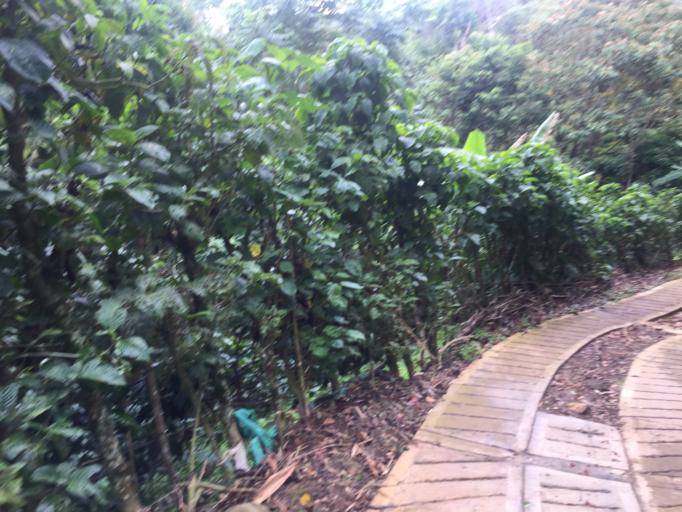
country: CO
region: Valle del Cauca
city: Cali
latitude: 3.4632
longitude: -76.6356
